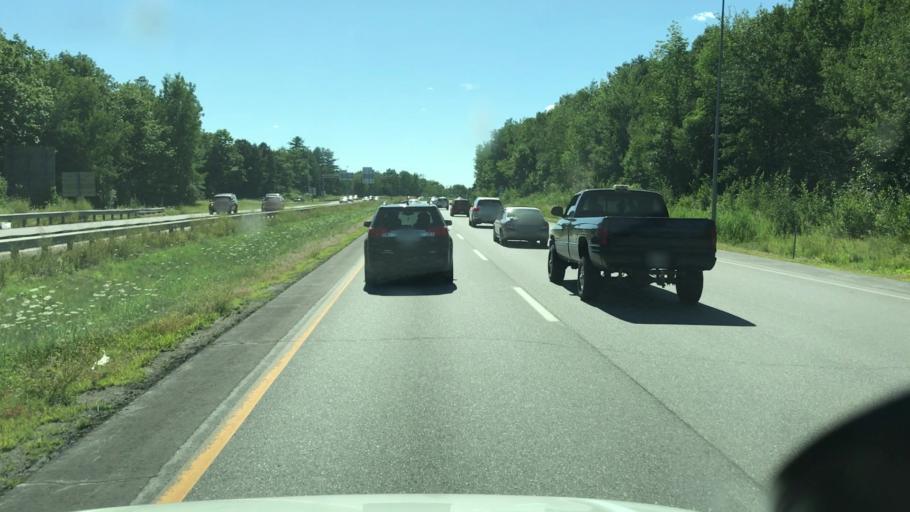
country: US
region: Maine
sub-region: Penobscot County
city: Bangor
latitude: 44.7867
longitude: -68.7948
